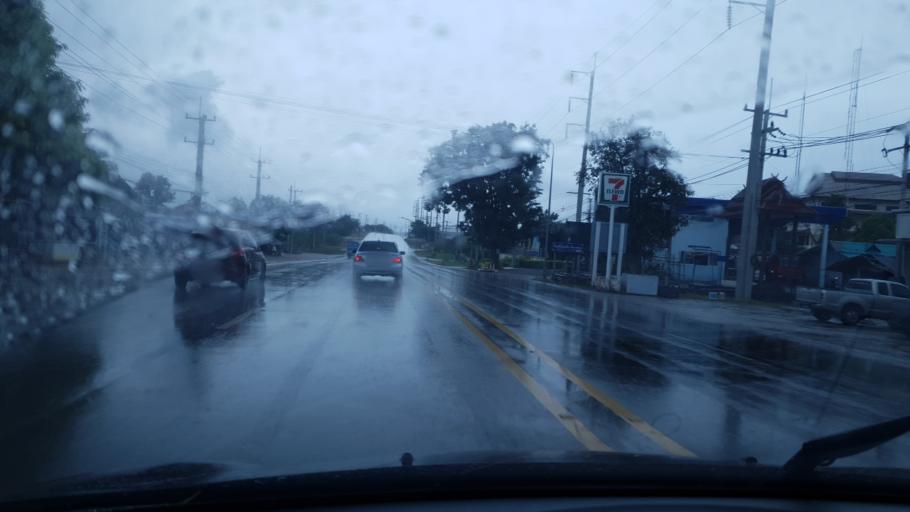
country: TH
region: Chiang Mai
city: Hot
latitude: 18.2096
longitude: 98.6161
